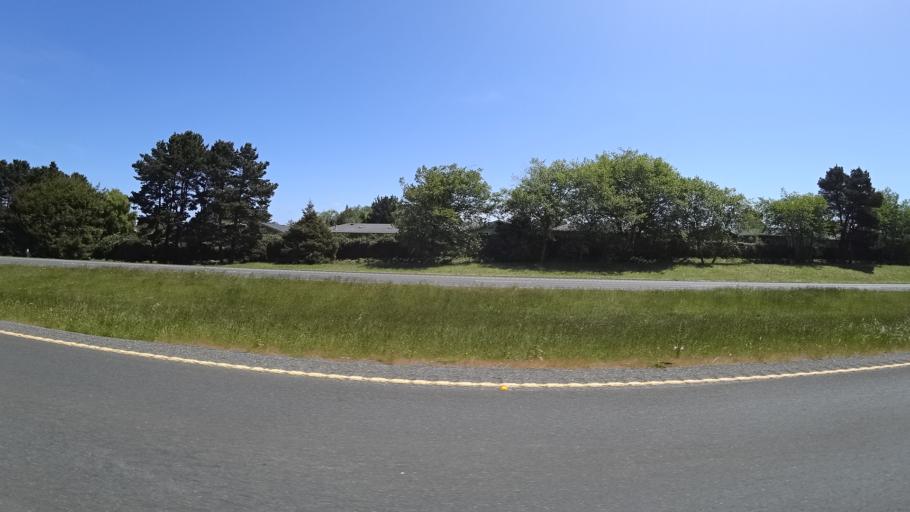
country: US
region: California
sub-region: Humboldt County
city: McKinleyville
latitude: 40.9438
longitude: -124.1164
